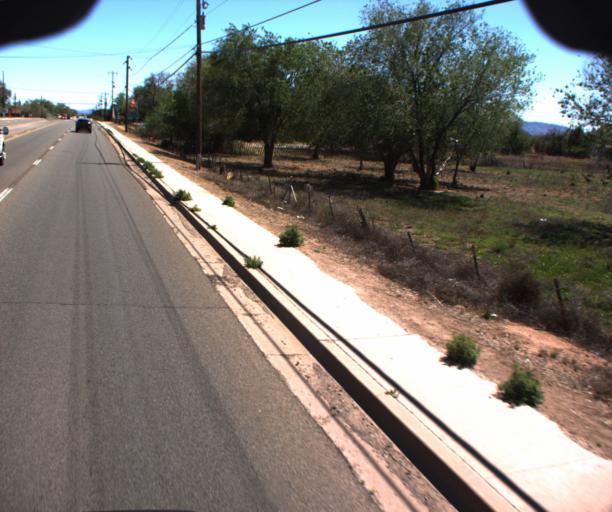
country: US
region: Arizona
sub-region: Yavapai County
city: Chino Valley
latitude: 34.7550
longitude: -112.4541
